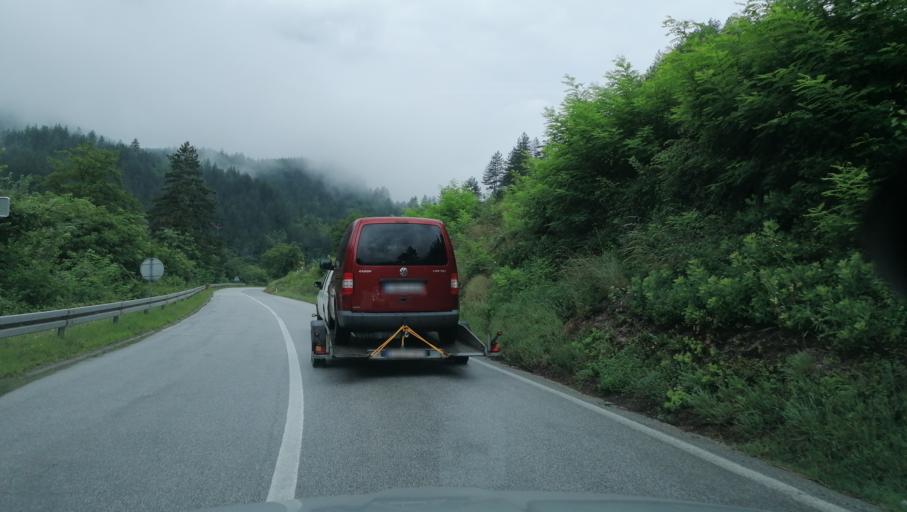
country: RS
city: Durici
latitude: 43.7796
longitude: 19.3686
